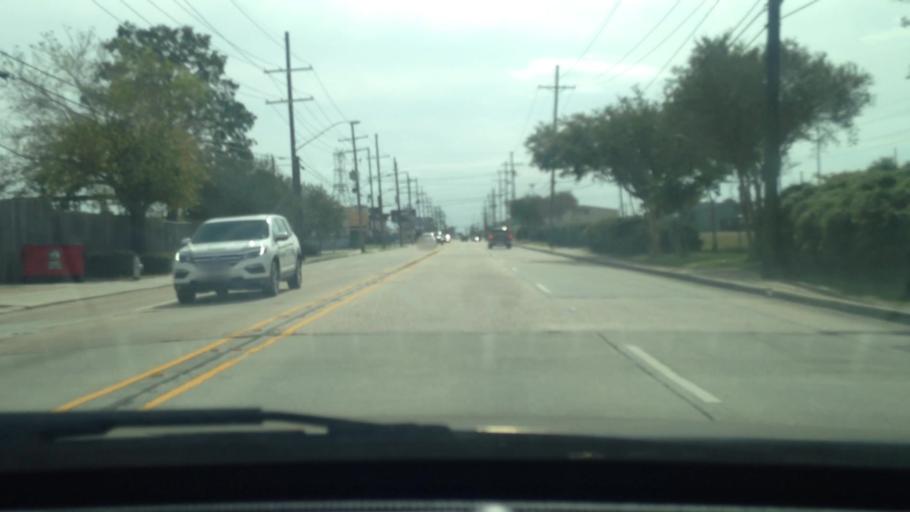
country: US
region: Louisiana
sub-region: Jefferson Parish
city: River Ridge
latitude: 29.9823
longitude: -90.2125
